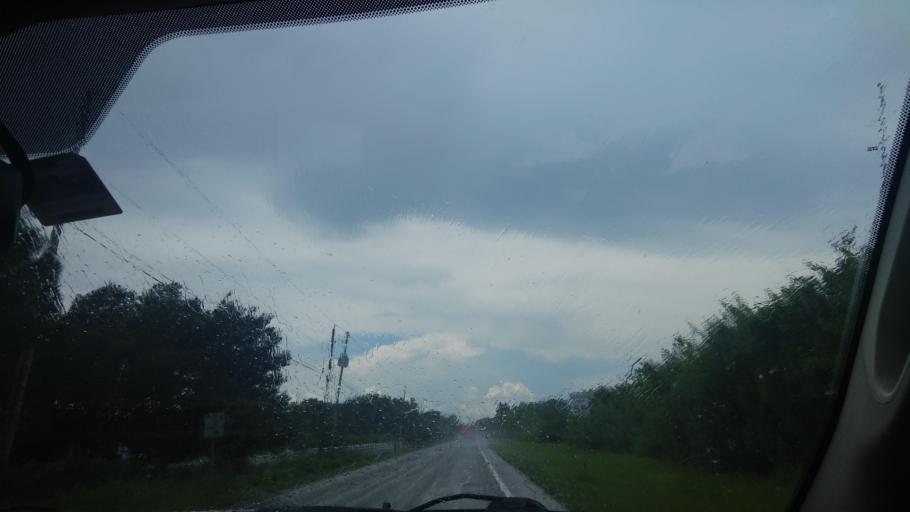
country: US
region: Florida
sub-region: Indian River County
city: Fellsmere
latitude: 27.8009
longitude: -80.6074
